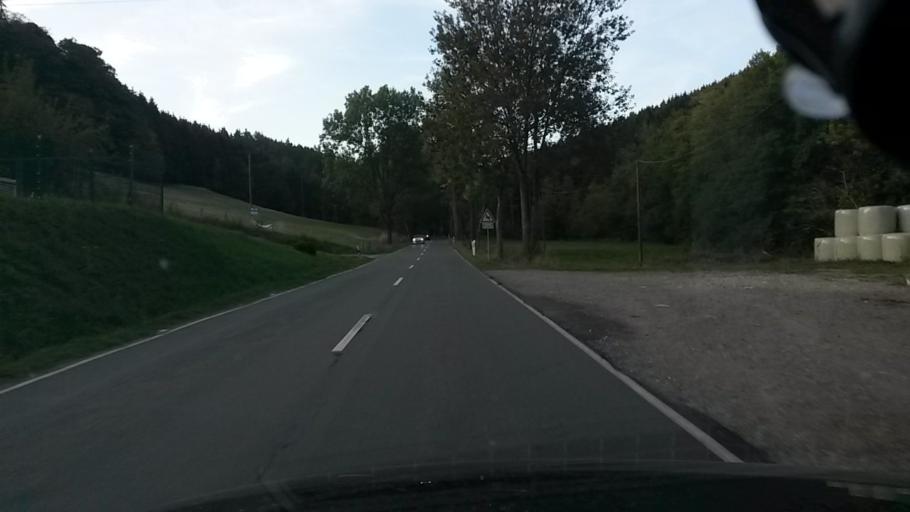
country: DE
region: North Rhine-Westphalia
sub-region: Regierungsbezirk Koln
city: Marienheide
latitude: 51.0605
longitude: 7.5155
